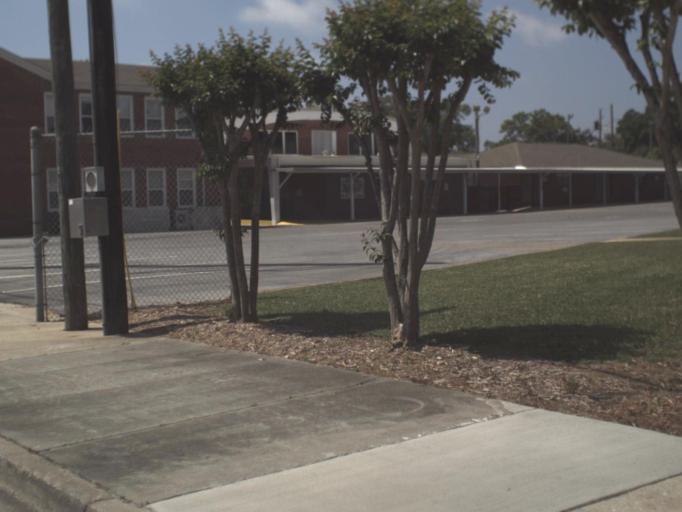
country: US
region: Florida
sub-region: Escambia County
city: Warrington
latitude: 30.3837
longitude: -87.2781
